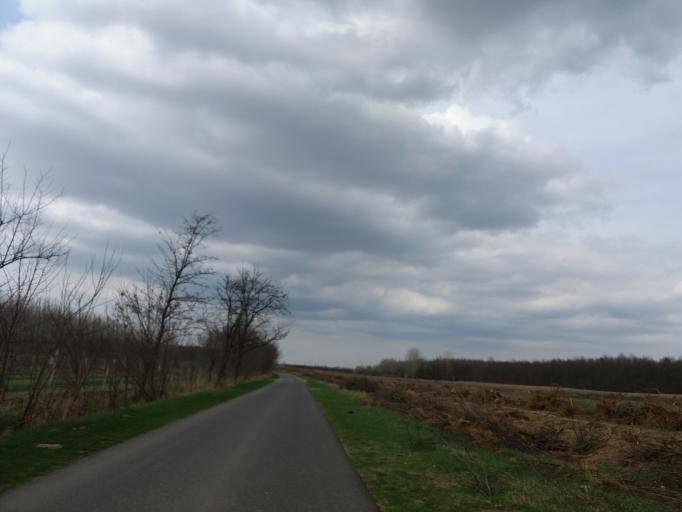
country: HU
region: Szabolcs-Szatmar-Bereg
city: Nyirtass
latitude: 48.0848
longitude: 22.0379
